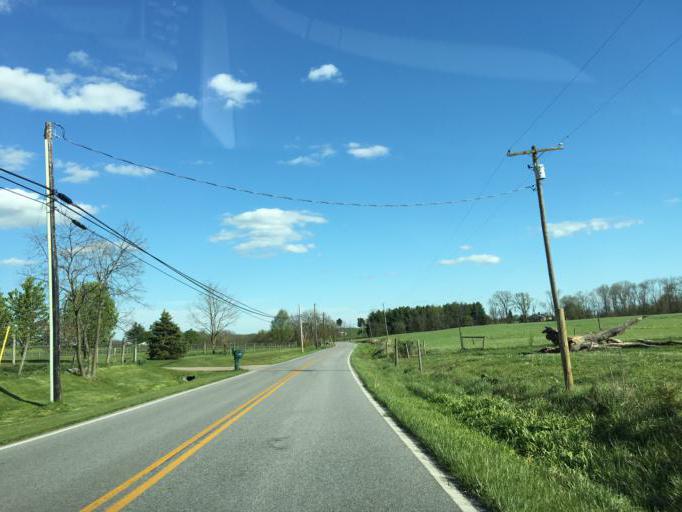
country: US
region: Maryland
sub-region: Frederick County
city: Emmitsburg
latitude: 39.6810
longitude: -77.3139
